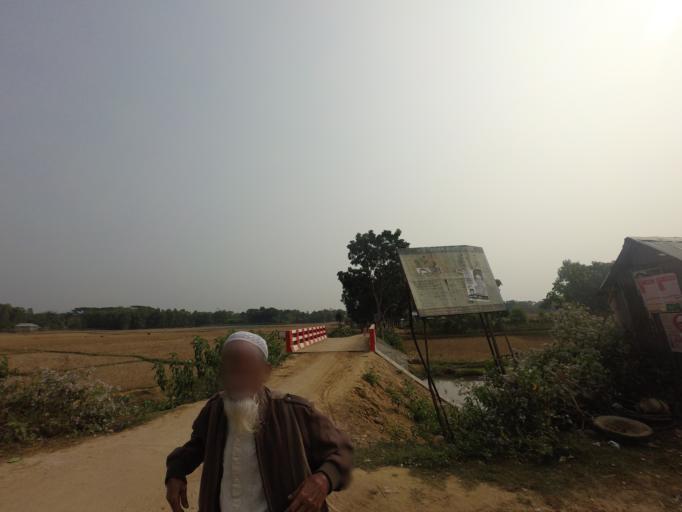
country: BD
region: Dhaka
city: Netrakona
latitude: 25.1566
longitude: 90.6589
